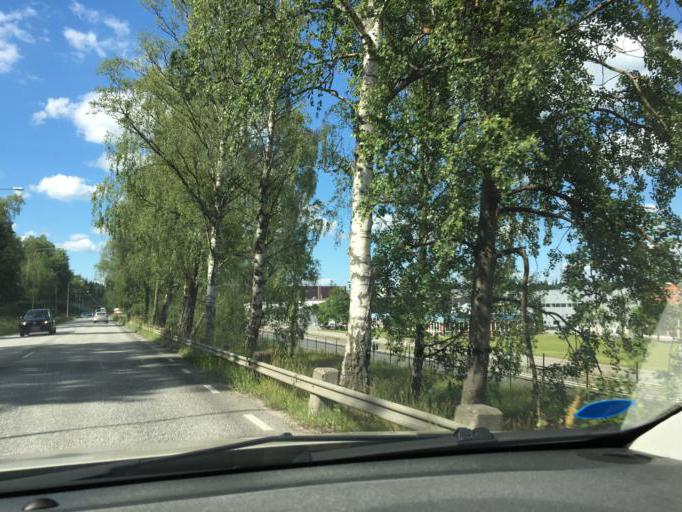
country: SE
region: Stockholm
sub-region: Sodertalje Kommun
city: Pershagen
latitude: 59.1695
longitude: 17.6381
